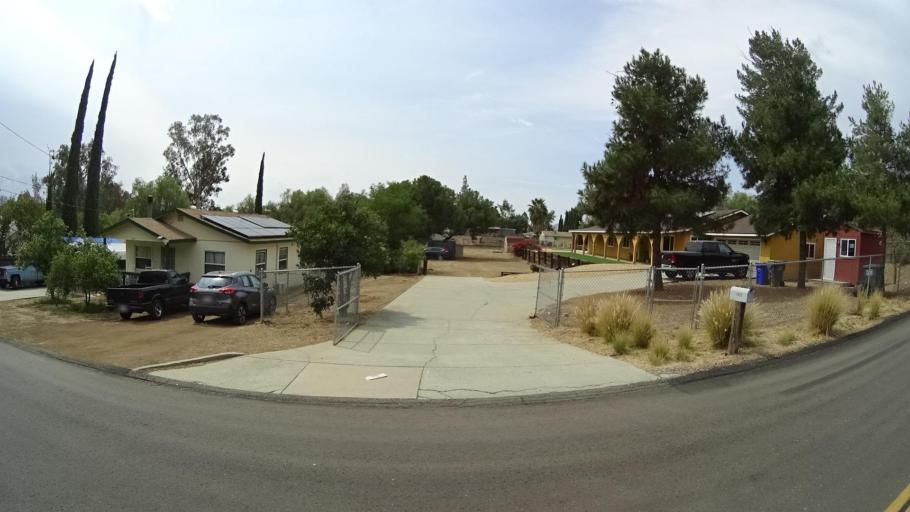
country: US
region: California
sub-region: San Diego County
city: Ramona
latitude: 33.0388
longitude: -116.8570
